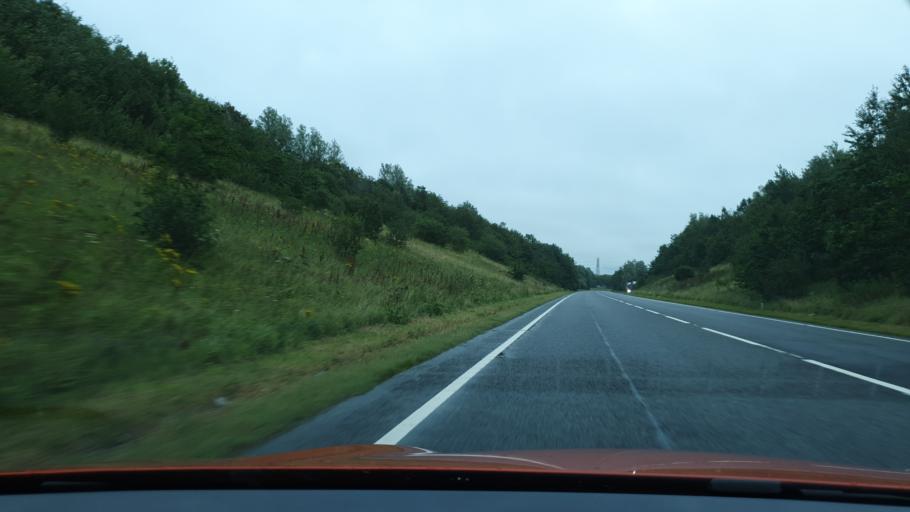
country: GB
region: England
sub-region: Cumbria
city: Dalton in Furness
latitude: 54.1649
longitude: -3.1720
